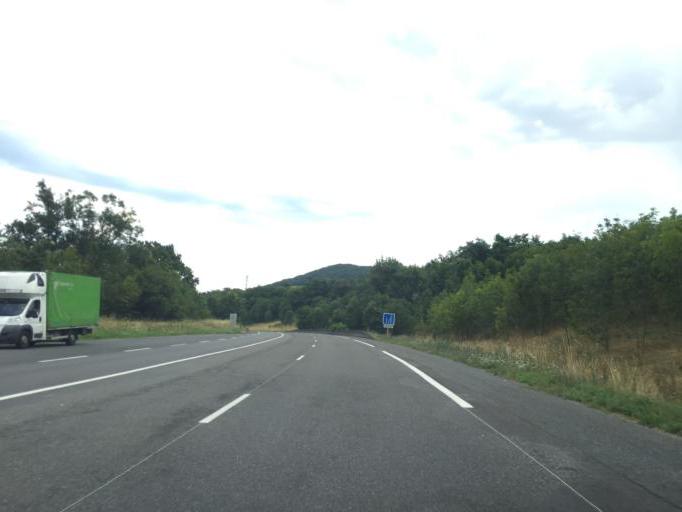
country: FR
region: Rhone-Alpes
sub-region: Departement du Rhone
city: Pontcharra-sur-Turdine
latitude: 45.8748
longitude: 4.4782
